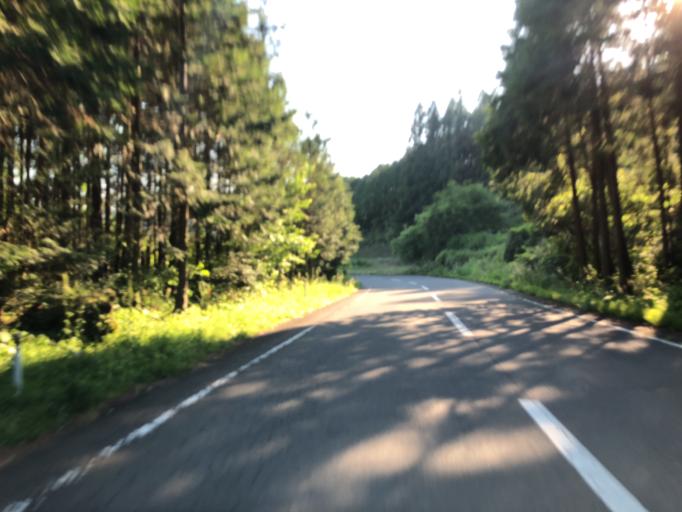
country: JP
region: Ibaraki
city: Daigo
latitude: 36.9249
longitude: 140.4621
